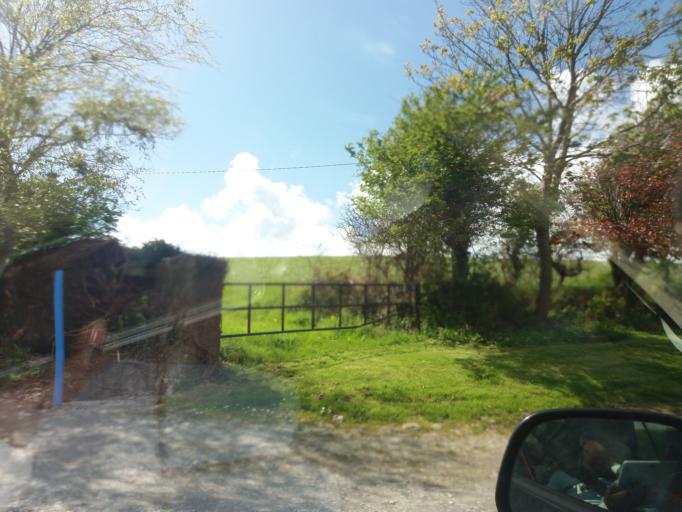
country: IE
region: Munster
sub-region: Waterford
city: Dunmore East
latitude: 52.2156
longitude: -6.9157
